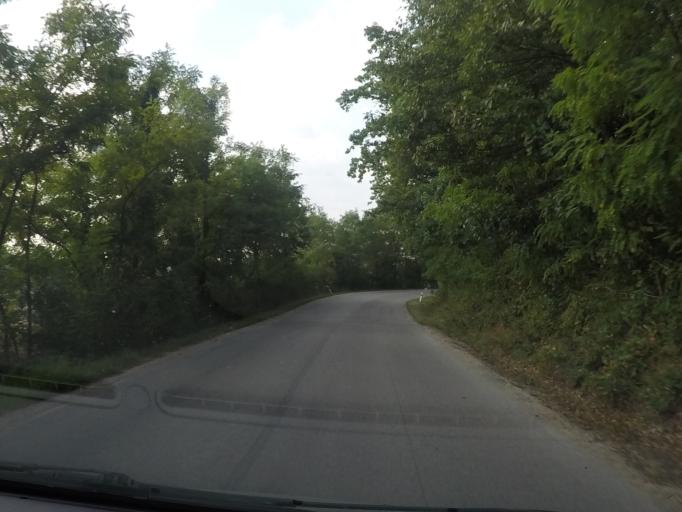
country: SK
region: Nitriansky
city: Zlate Moravce
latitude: 48.4422
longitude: 18.3212
